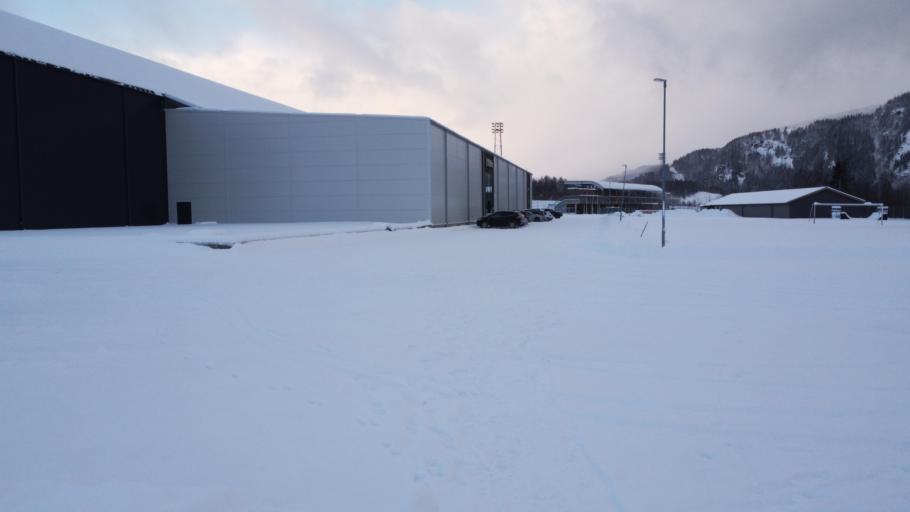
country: NO
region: Nordland
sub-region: Rana
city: Mo i Rana
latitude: 66.3212
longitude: 14.1613
